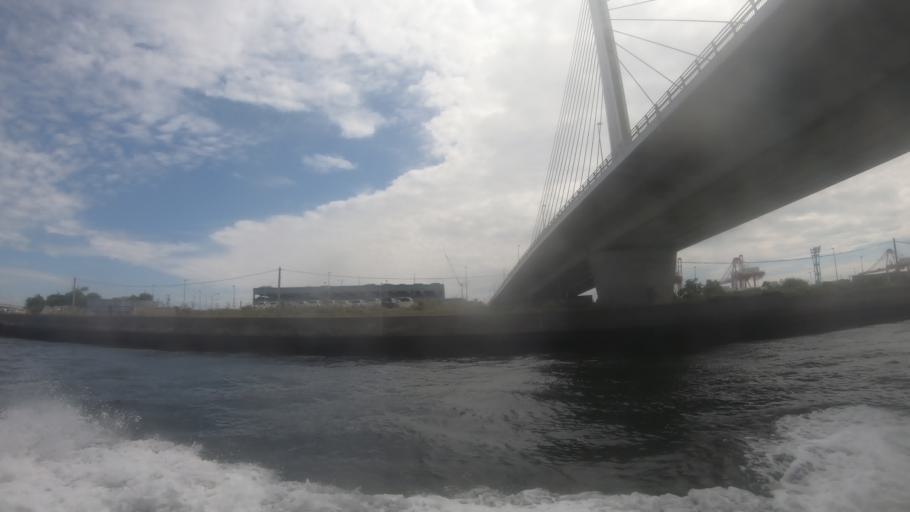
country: JP
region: Kanagawa
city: Yokohama
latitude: 35.4094
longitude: 139.6785
